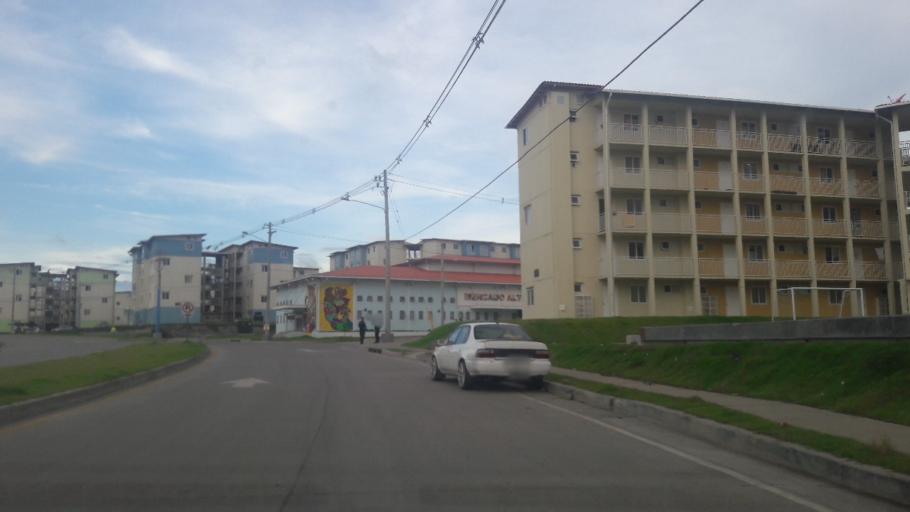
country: PA
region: Colon
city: Cativa
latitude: 9.3706
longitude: -79.8508
